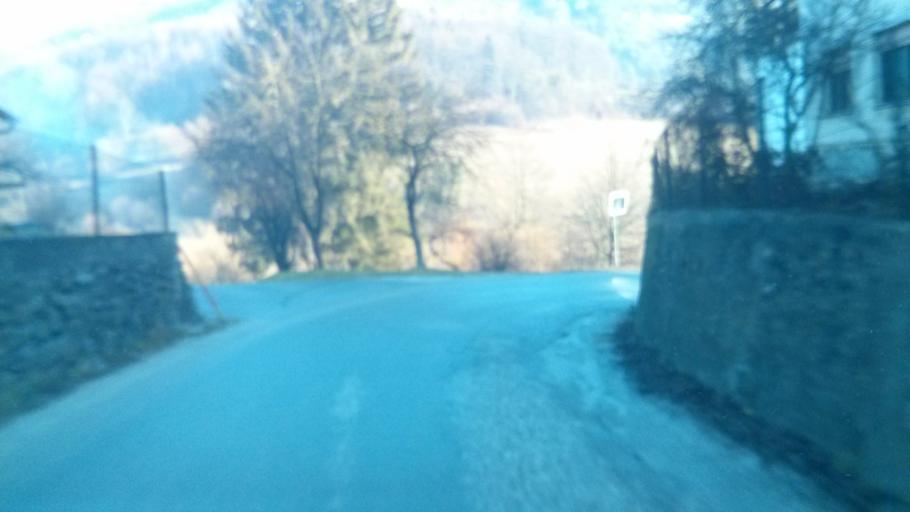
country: SI
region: Trebnje
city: Mirna
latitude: 45.9994
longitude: 14.9797
